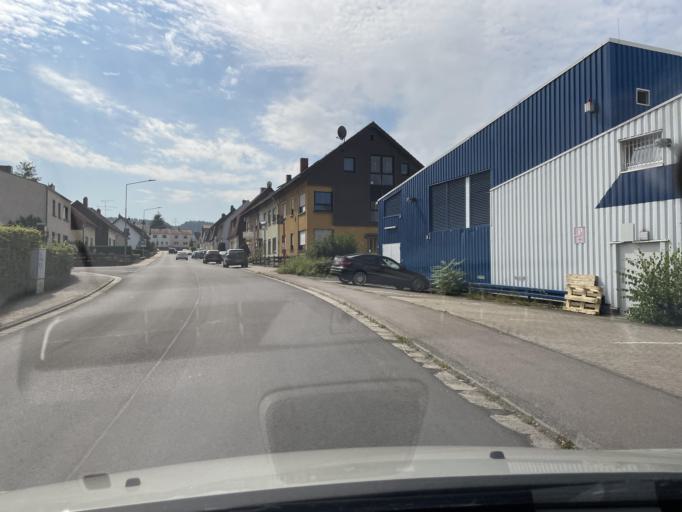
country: DE
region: Saarland
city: Spiesen-Elversberg
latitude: 49.2879
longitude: 7.1527
